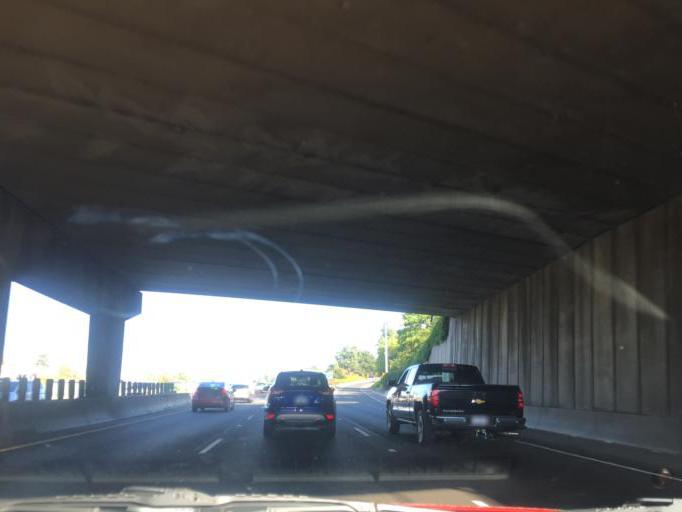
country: US
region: Oregon
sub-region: Multnomah County
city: Lents
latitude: 45.5334
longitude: -122.5792
